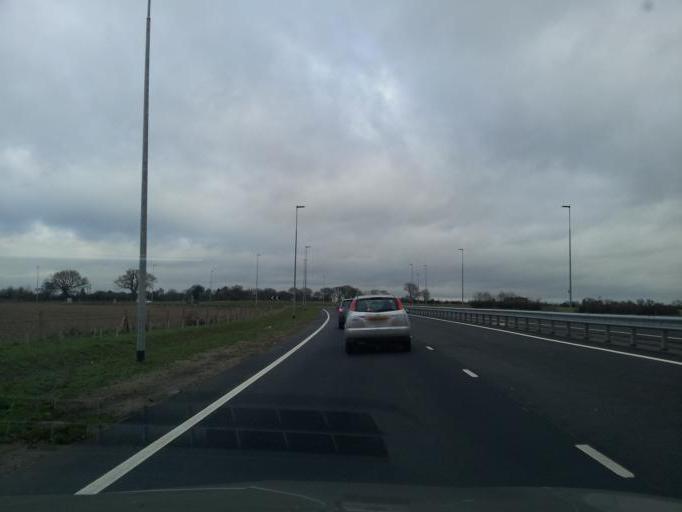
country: GB
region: England
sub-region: Norfolk
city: Surlingham
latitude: 52.6301
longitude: 1.3865
